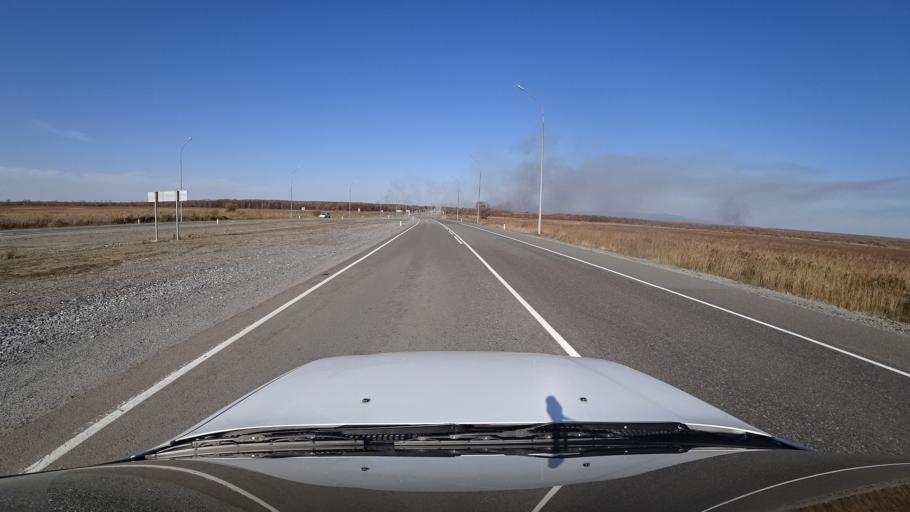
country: RU
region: Primorskiy
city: Lazo
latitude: 45.8631
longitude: 133.7200
